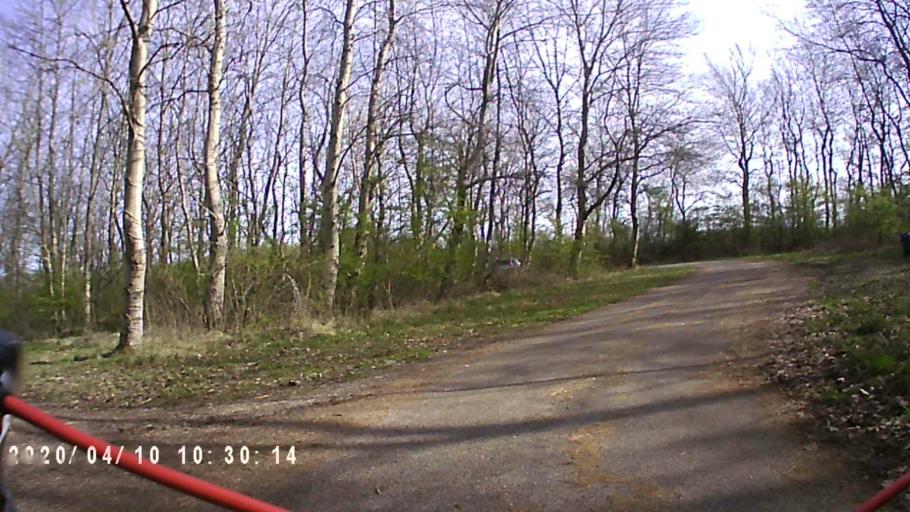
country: NL
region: Friesland
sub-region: Gemeente Dongeradeel
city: Anjum
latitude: 53.3923
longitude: 6.2123
